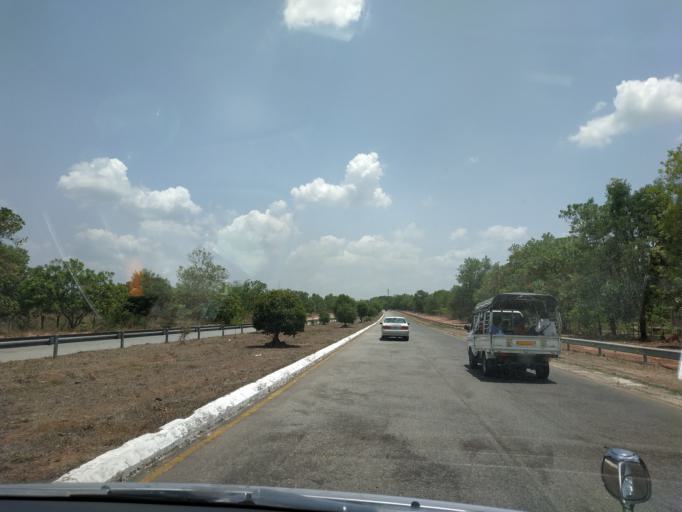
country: MM
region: Bago
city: Thanatpin
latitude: 17.1967
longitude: 96.1933
